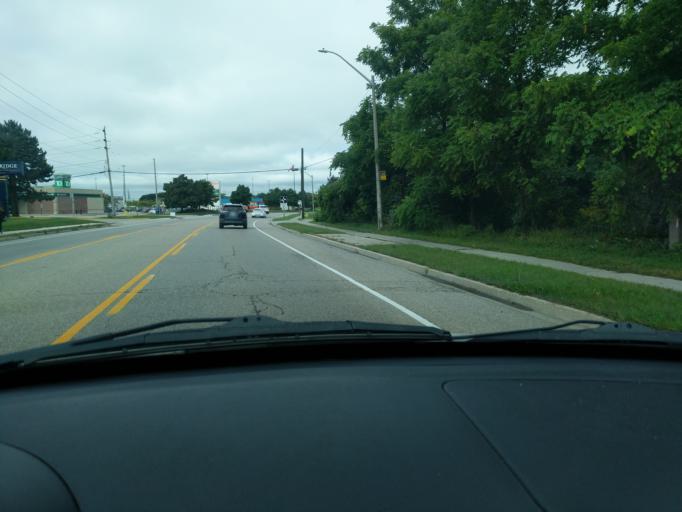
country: CA
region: Ontario
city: Cambridge
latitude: 43.4165
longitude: -80.3211
